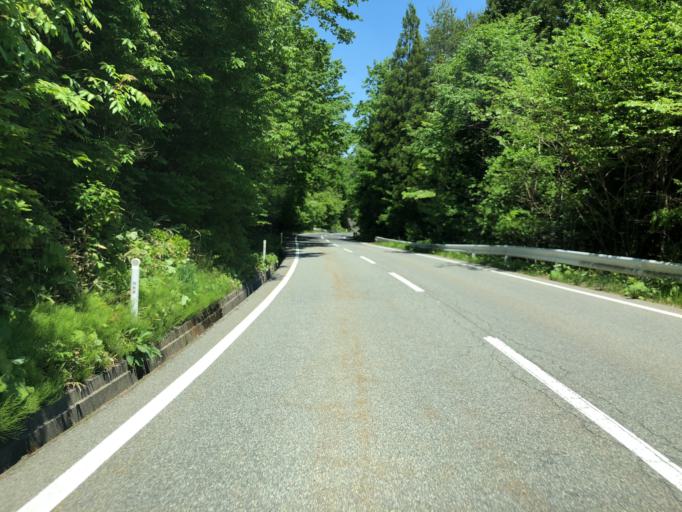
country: JP
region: Fukushima
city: Namie
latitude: 37.5234
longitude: 140.8003
